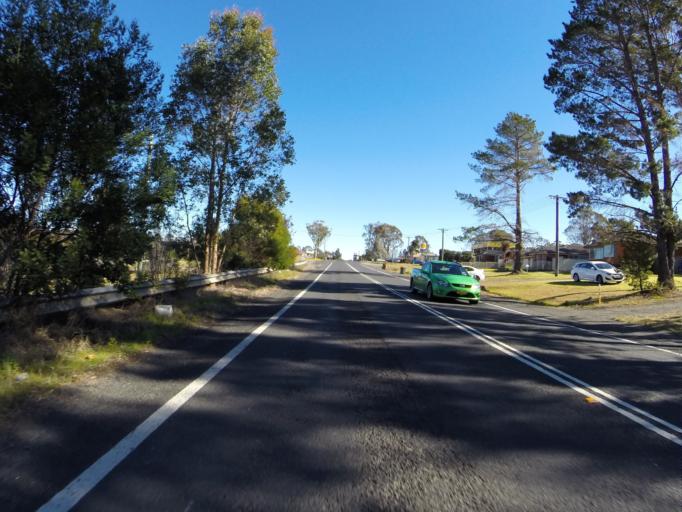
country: AU
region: New South Wales
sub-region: Wollondilly
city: Douglas Park
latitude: -34.2410
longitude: 150.7004
